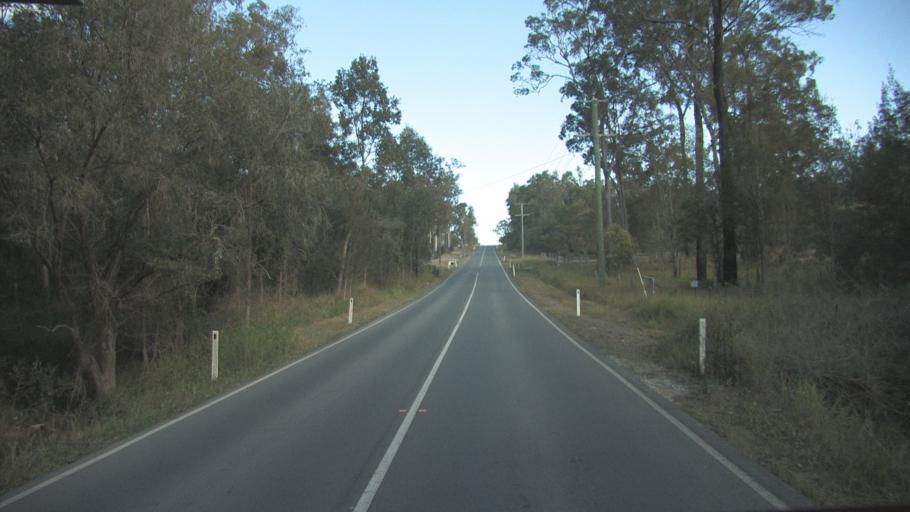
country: AU
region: Queensland
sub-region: Logan
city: Cedar Vale
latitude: -27.8276
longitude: 153.0535
